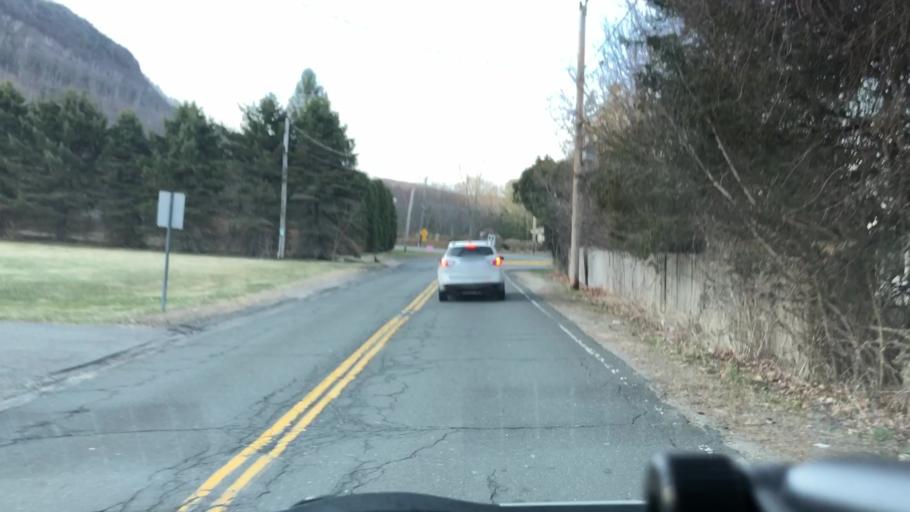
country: US
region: Massachusetts
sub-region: Hampshire County
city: Easthampton
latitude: 42.2516
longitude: -72.6538
